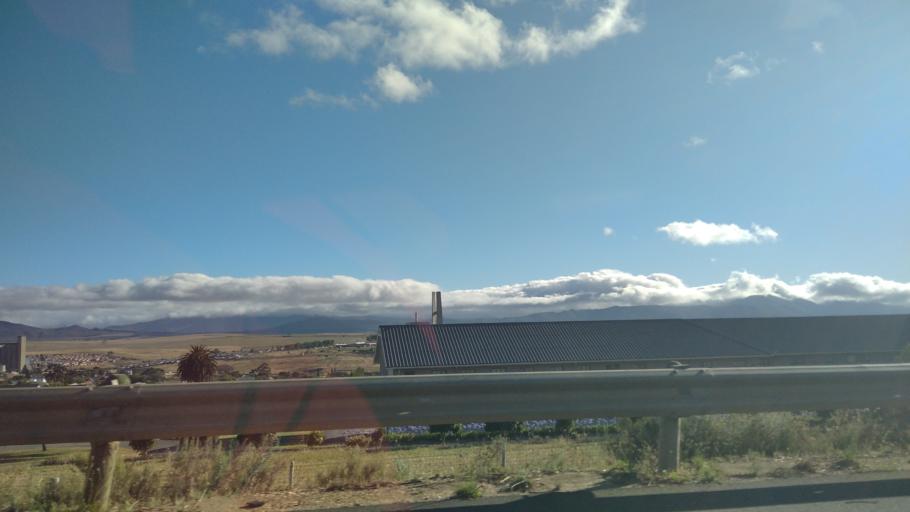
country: ZA
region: Western Cape
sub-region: Overberg District Municipality
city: Caledon
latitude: -34.2277
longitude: 19.4255
